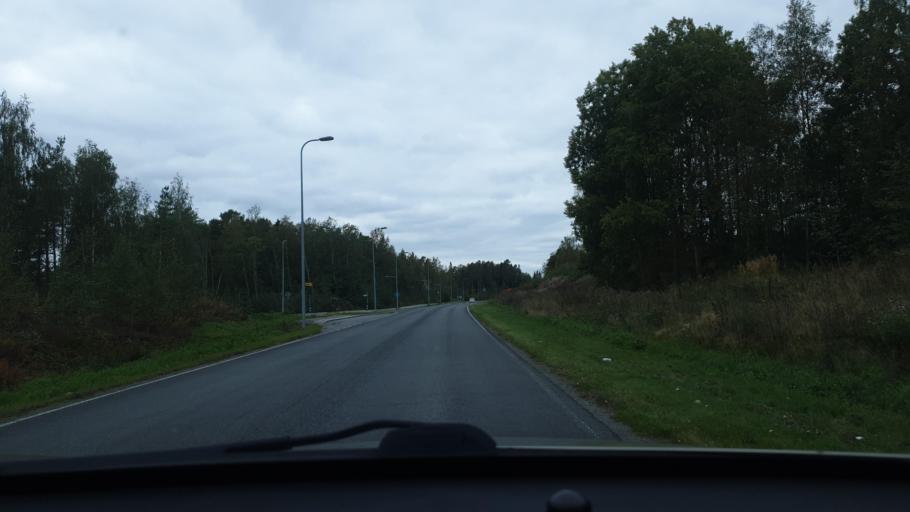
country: FI
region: Ostrobothnia
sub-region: Vaasa
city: Teeriniemi
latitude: 63.1017
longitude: 21.6877
